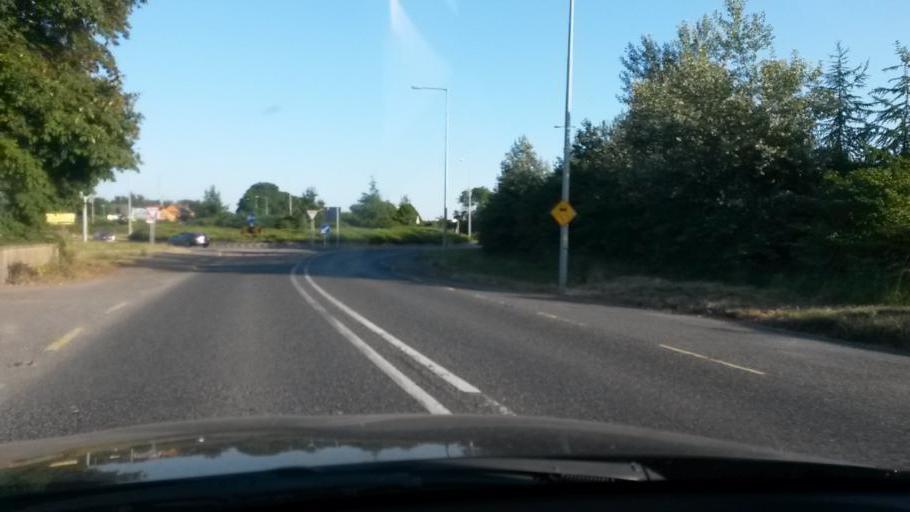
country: IE
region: Leinster
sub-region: Dublin City
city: Finglas
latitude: 53.4354
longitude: -6.3344
